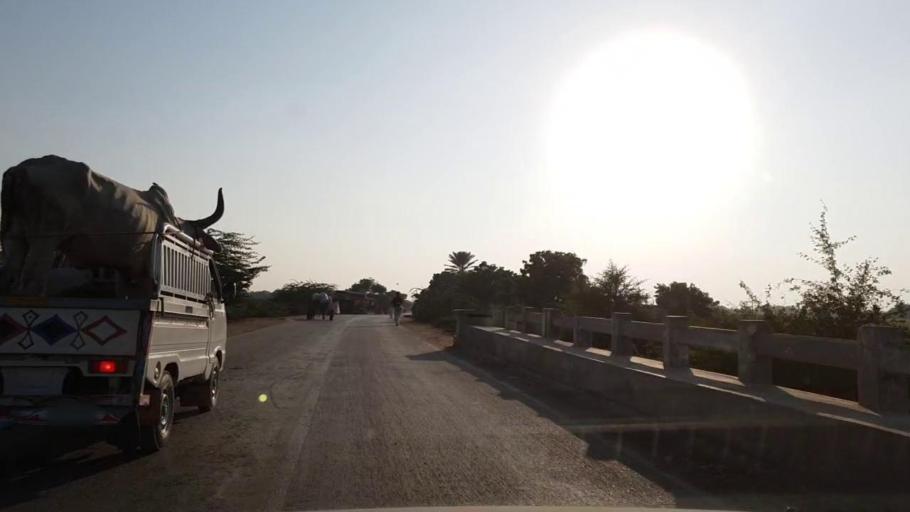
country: PK
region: Sindh
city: Mirpur Batoro
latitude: 24.6894
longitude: 68.1775
